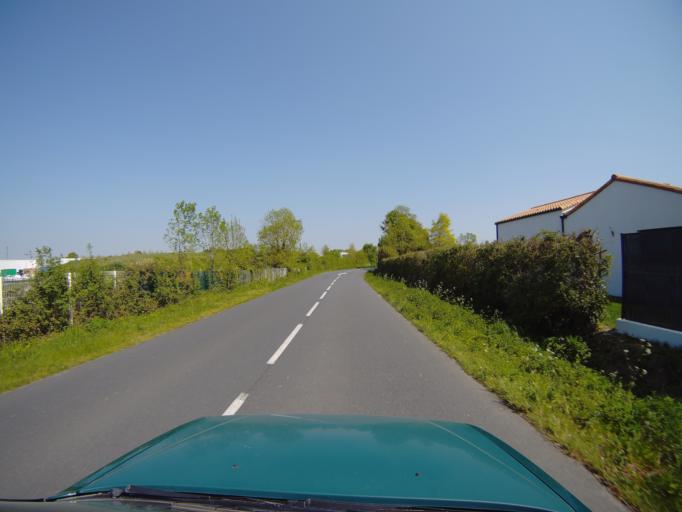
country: FR
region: Pays de la Loire
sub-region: Departement de la Vendee
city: Bouffere
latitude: 46.9515
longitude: -1.3520
